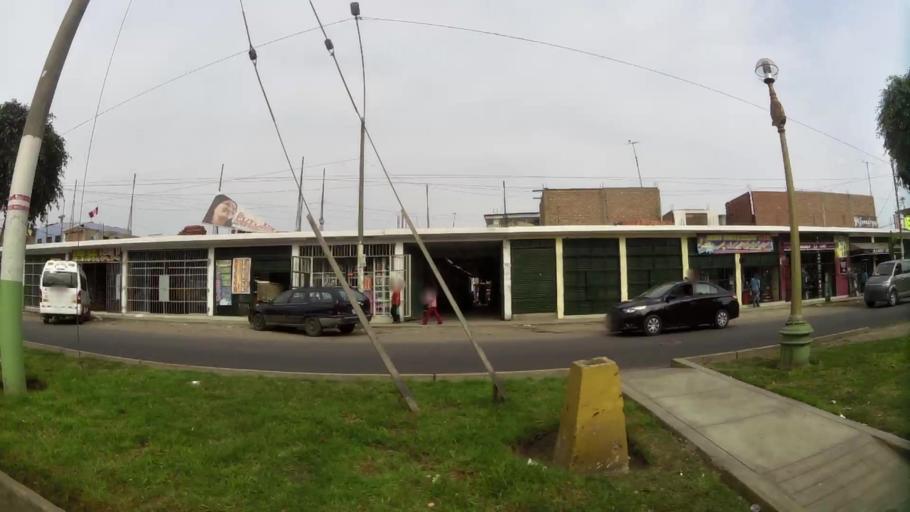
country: PE
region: Callao
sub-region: Callao
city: Callao
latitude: -12.0268
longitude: -77.1000
